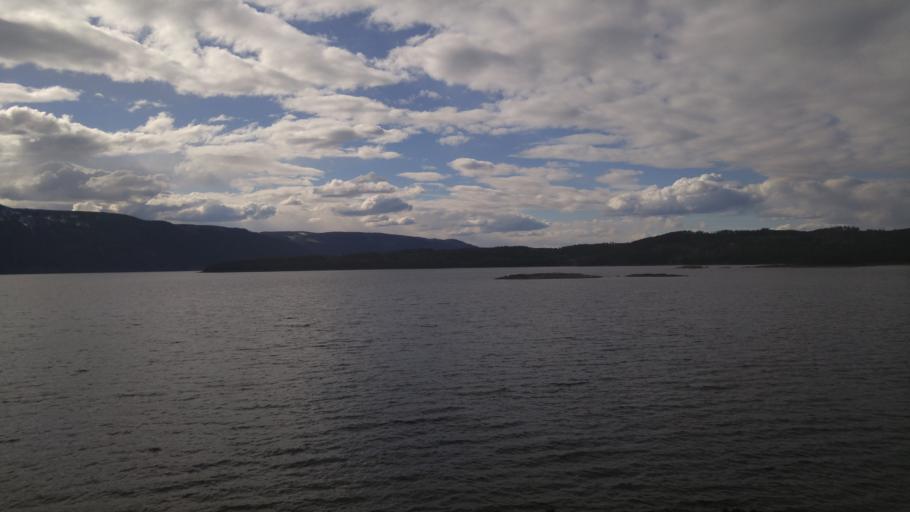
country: NO
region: Hedmark
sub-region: Stange
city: Stange
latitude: 60.5771
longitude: 11.2669
